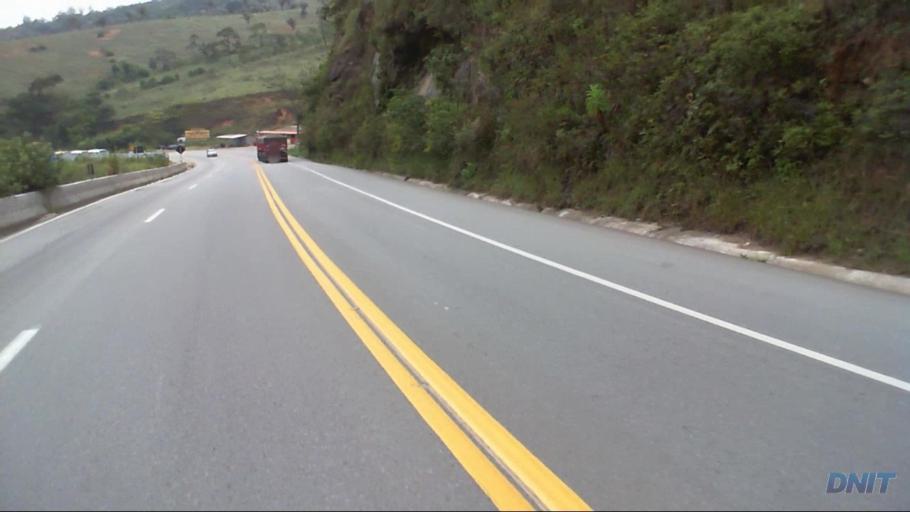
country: BR
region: Minas Gerais
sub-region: Nova Era
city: Nova Era
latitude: -19.6515
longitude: -42.9459
